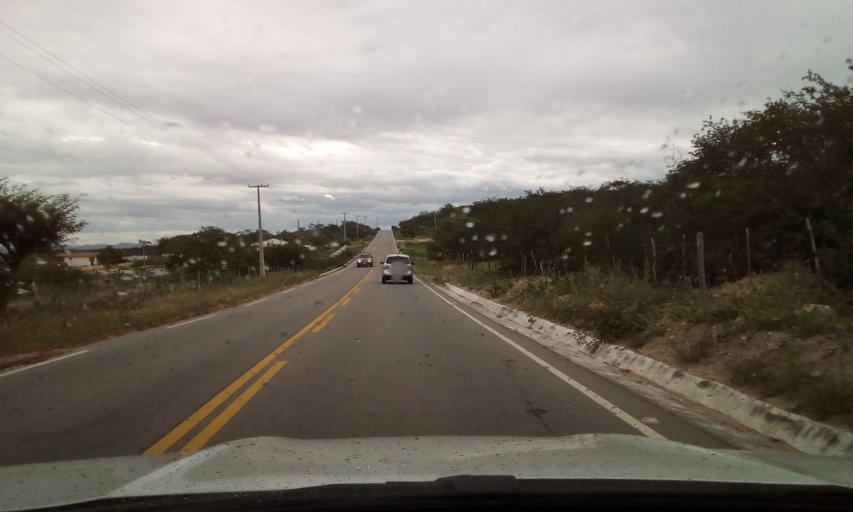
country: BR
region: Paraiba
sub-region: Picui
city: Picui
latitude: -6.5741
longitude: -36.2657
